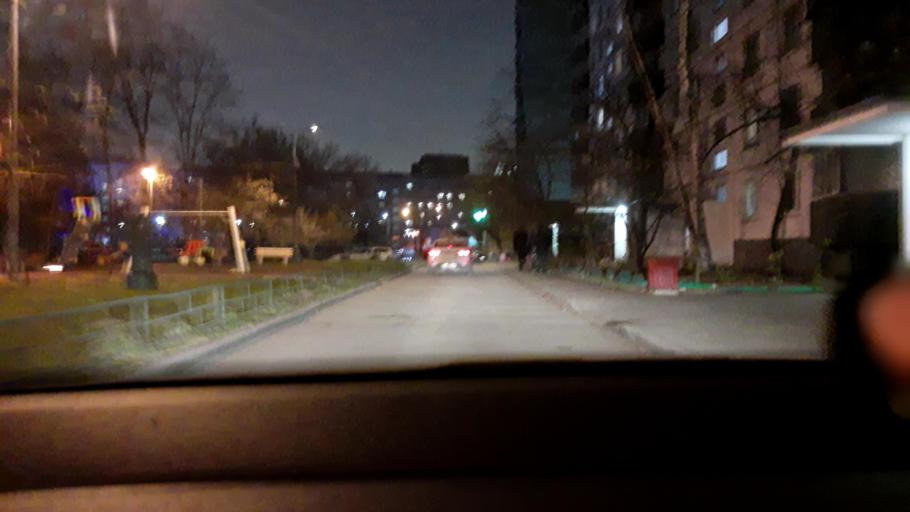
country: RU
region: Moscow
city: Likhobory
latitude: 55.8278
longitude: 37.5691
